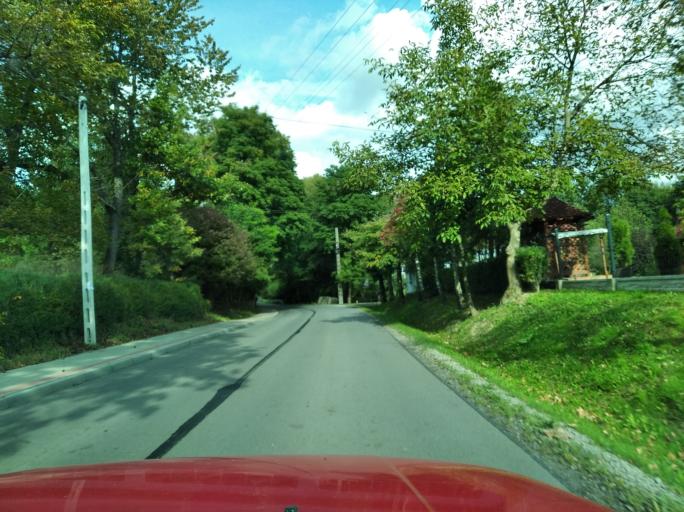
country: PL
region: Subcarpathian Voivodeship
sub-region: Powiat rzeszowski
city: Tyczyn
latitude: 49.9545
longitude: 22.0298
